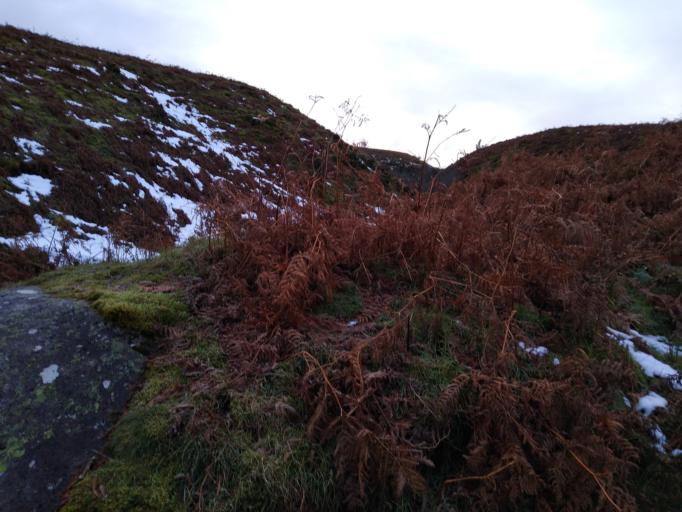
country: GB
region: England
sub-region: Cumbria
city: Penrith
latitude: 54.5903
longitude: -2.8168
